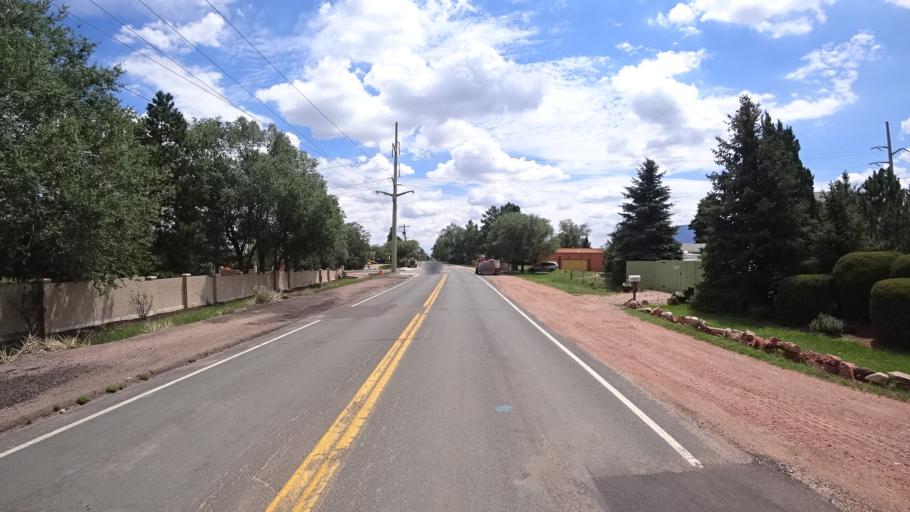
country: US
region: Colorado
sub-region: El Paso County
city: Colorado Springs
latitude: 38.8614
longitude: -104.8498
